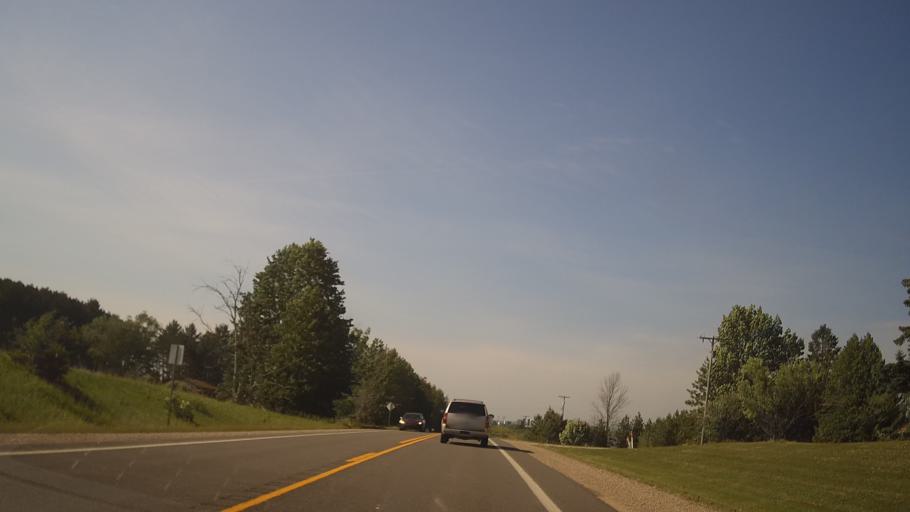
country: US
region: Michigan
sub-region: Ogemaw County
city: West Branch
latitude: 44.3370
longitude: -84.1257
